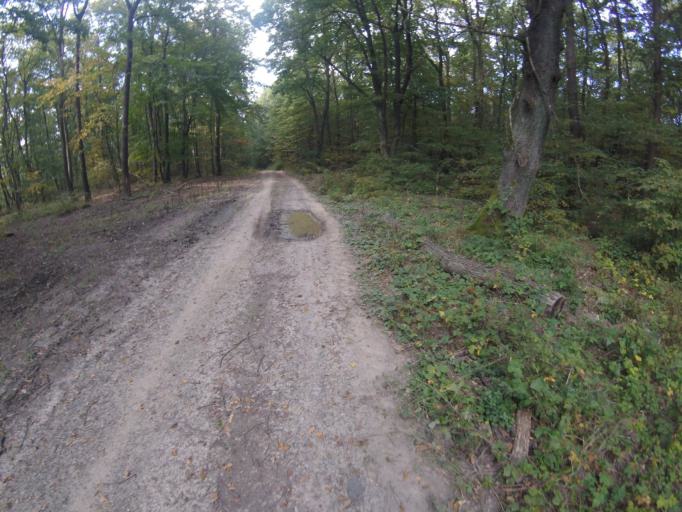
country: HU
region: Komarom-Esztergom
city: Kesztolc
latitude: 47.7723
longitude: 18.8133
